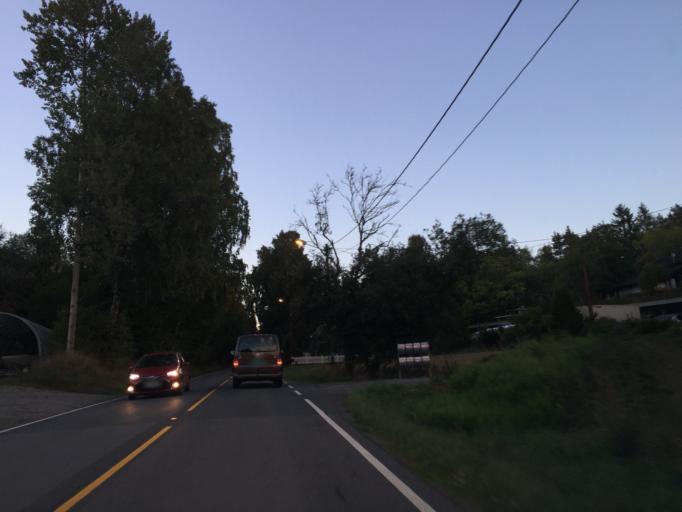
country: NO
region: Ostfold
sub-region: Moss
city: Moss
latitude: 59.4839
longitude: 10.6970
